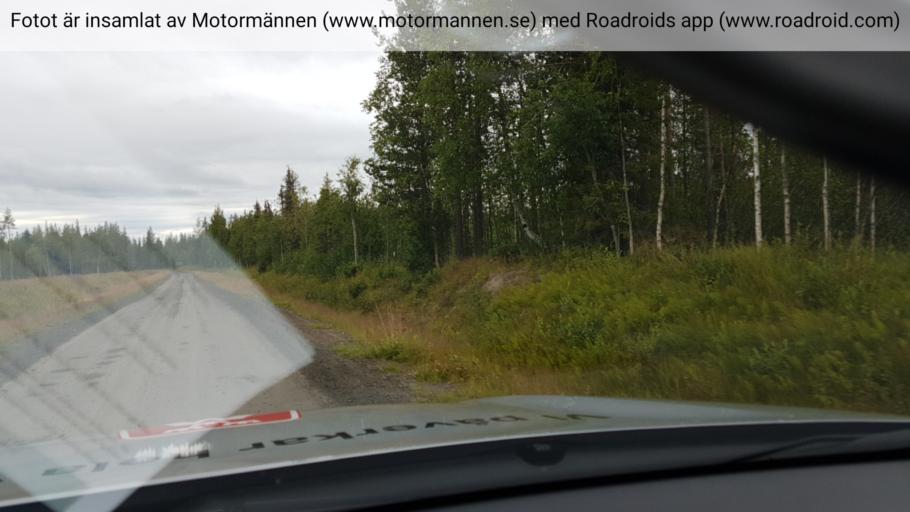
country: SE
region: Norrbotten
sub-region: Pajala Kommun
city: Pajala
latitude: 67.0133
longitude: 22.8536
